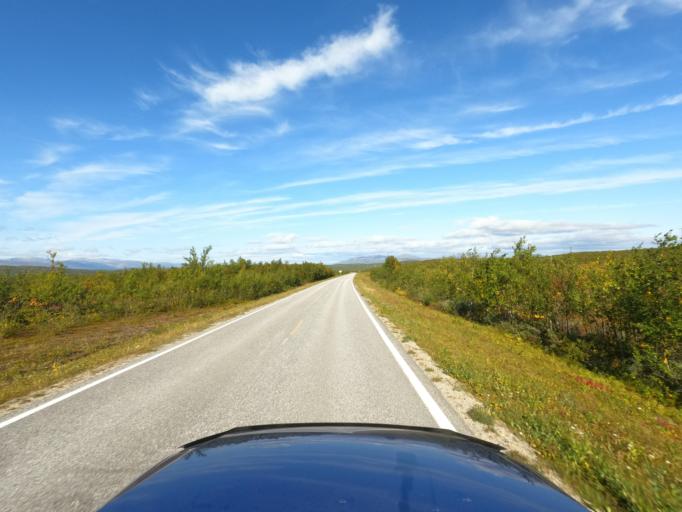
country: NO
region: Finnmark Fylke
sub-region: Karasjok
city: Karasjohka
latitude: 69.7271
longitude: 25.2345
